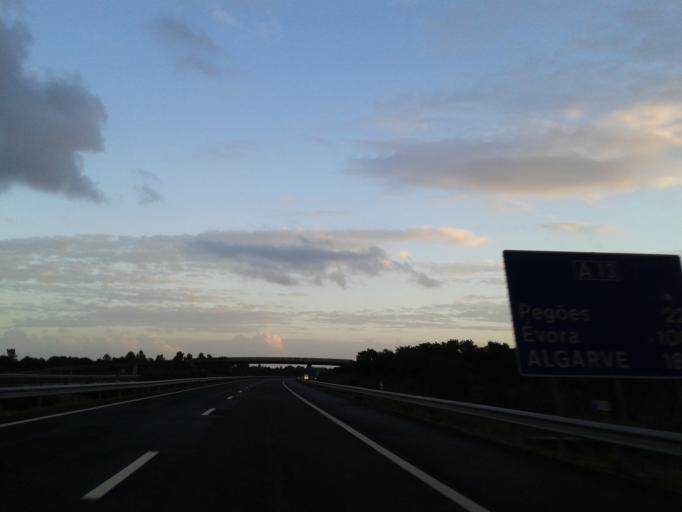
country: PT
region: Santarem
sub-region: Benavente
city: Poceirao
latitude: 38.8325
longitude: -8.7212
